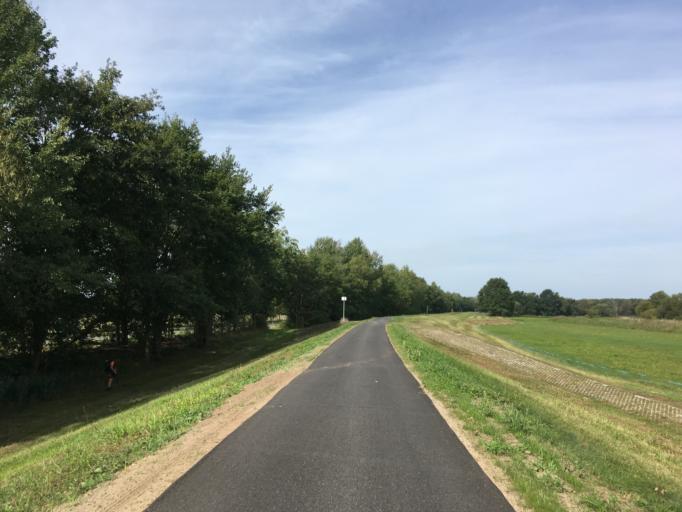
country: DE
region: Brandenburg
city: Heinersbruck
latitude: 51.8179
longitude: 14.5945
